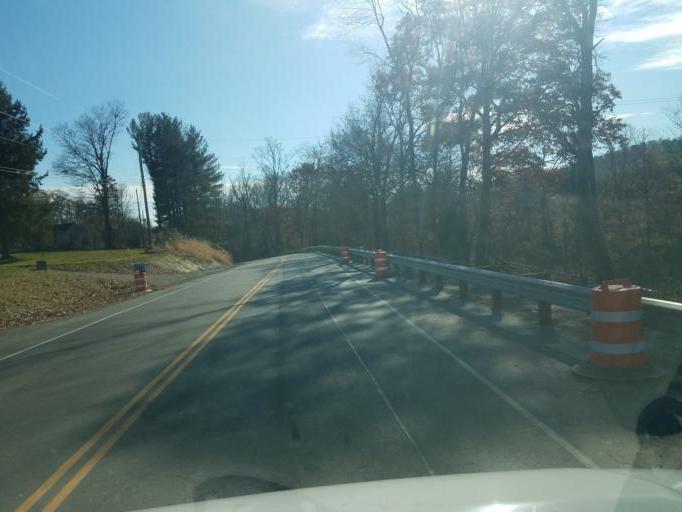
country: US
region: Ohio
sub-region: Scioto County
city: Sciotodale
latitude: 38.8383
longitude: -82.8521
